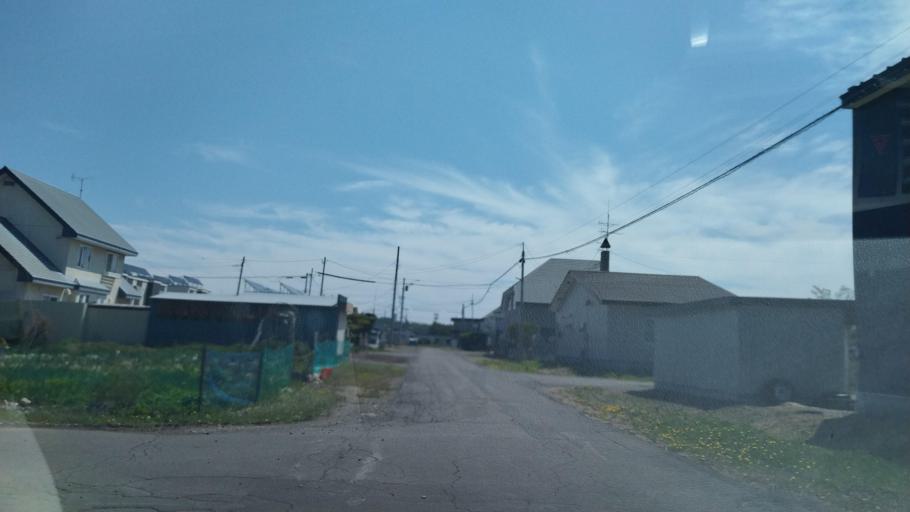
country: JP
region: Hokkaido
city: Otofuke
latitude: 43.2386
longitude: 143.2913
